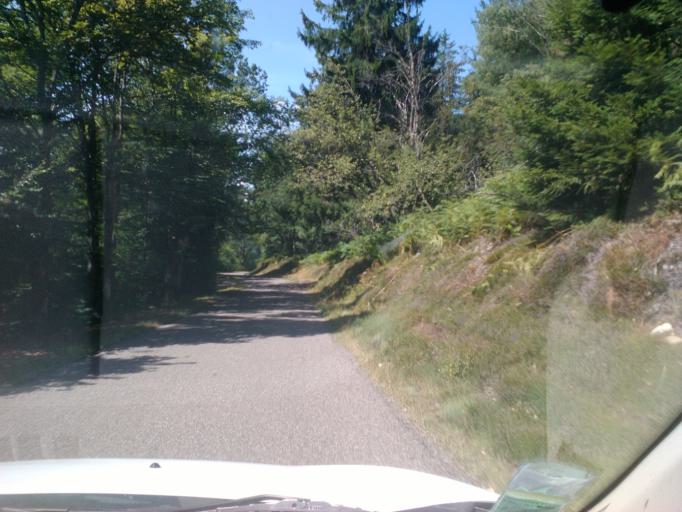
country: FR
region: Lorraine
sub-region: Departement des Vosges
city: Le Tholy
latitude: 48.0647
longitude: 6.7533
